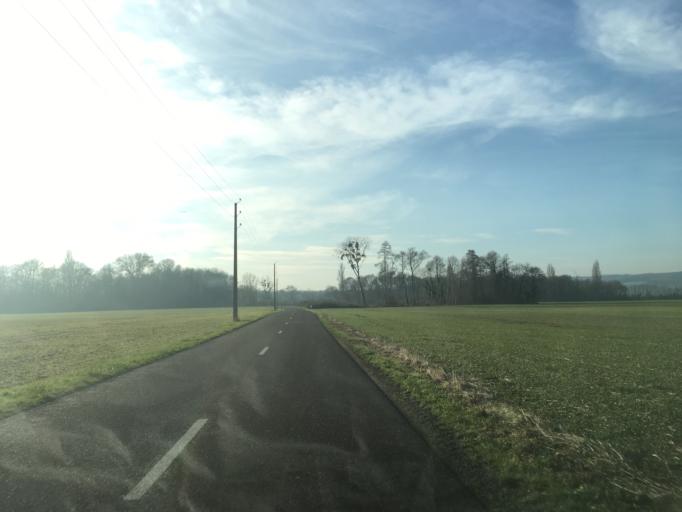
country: FR
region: Haute-Normandie
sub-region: Departement de l'Eure
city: Houlbec-Cocherel
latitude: 49.0555
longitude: 1.3270
